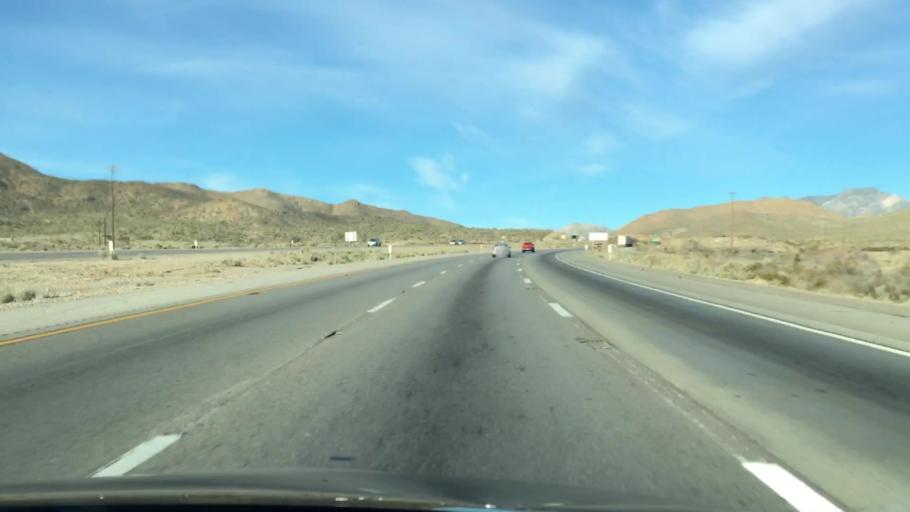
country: US
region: Nevada
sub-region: Clark County
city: Sandy Valley
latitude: 35.4618
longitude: -115.4753
